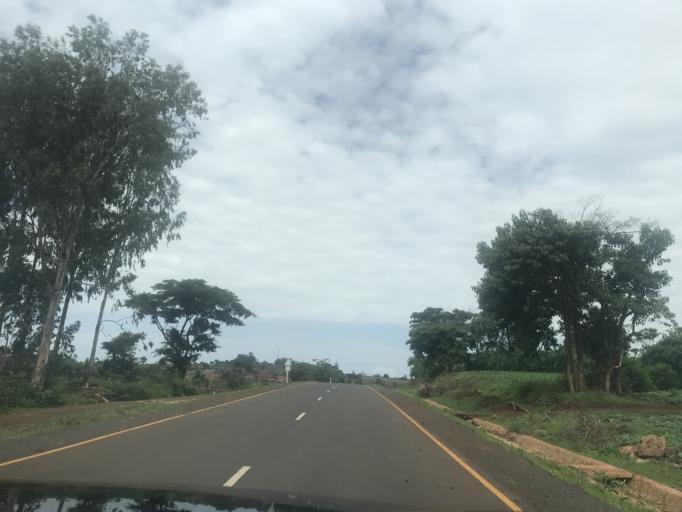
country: ET
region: Oromiya
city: Shambu
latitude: 9.8741
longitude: 36.7008
